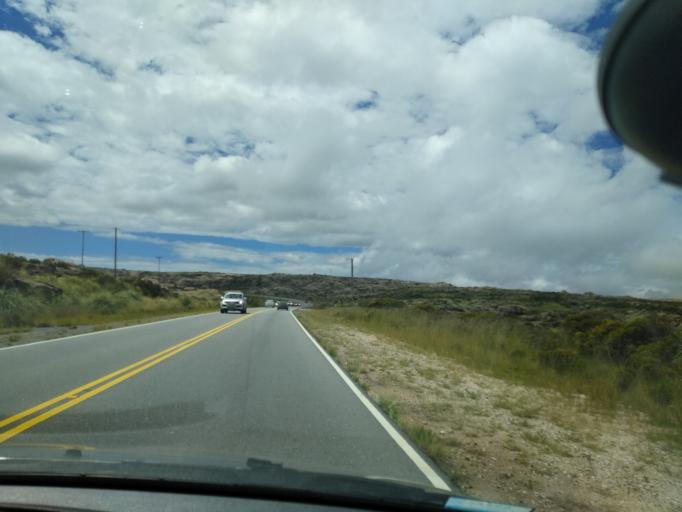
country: AR
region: Cordoba
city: Villa Cura Brochero
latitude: -31.6155
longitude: -64.8989
